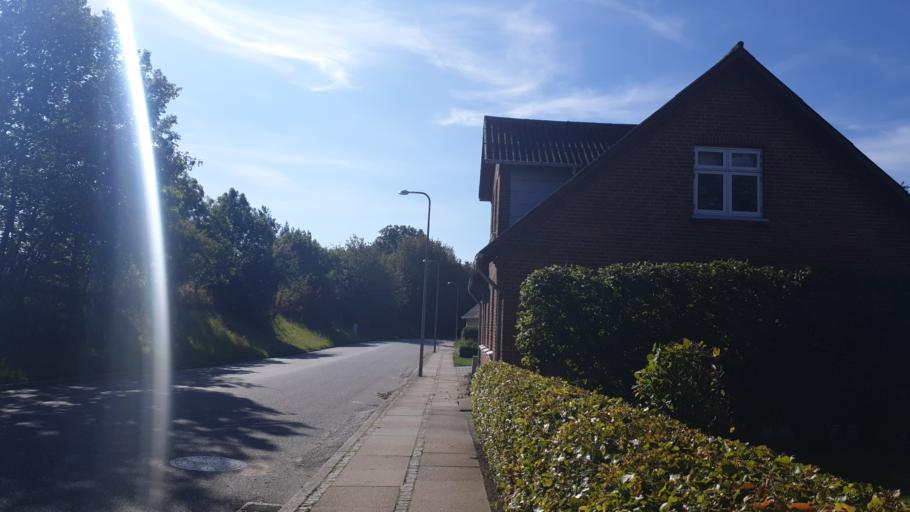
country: DK
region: Central Jutland
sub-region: Hedensted Kommune
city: Hedensted
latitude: 55.8010
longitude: 9.7005
